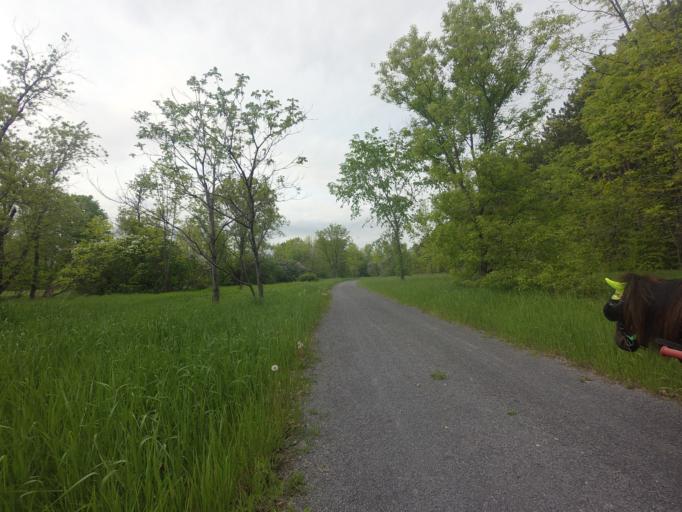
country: CA
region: Ontario
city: Kingston
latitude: 44.3613
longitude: -76.6271
